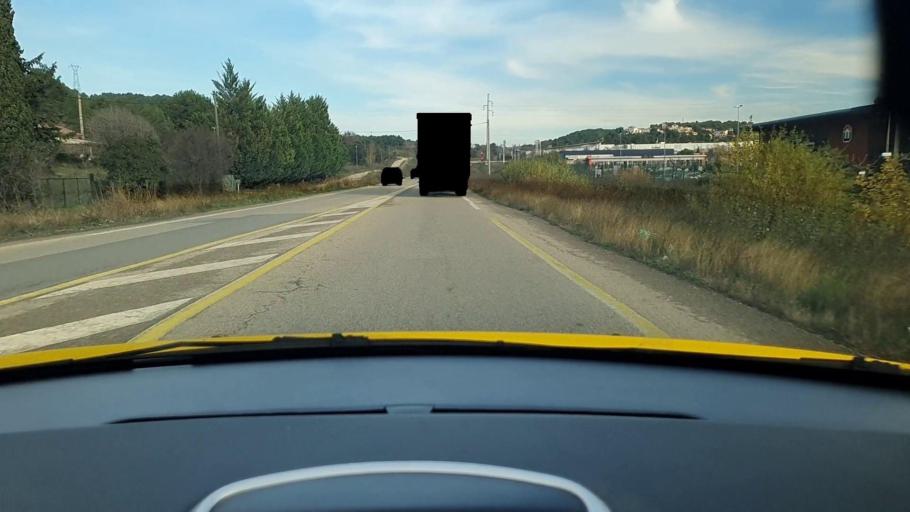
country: FR
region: Languedoc-Roussillon
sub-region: Departement du Gard
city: Beaucaire
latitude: 43.8106
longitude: 4.6109
